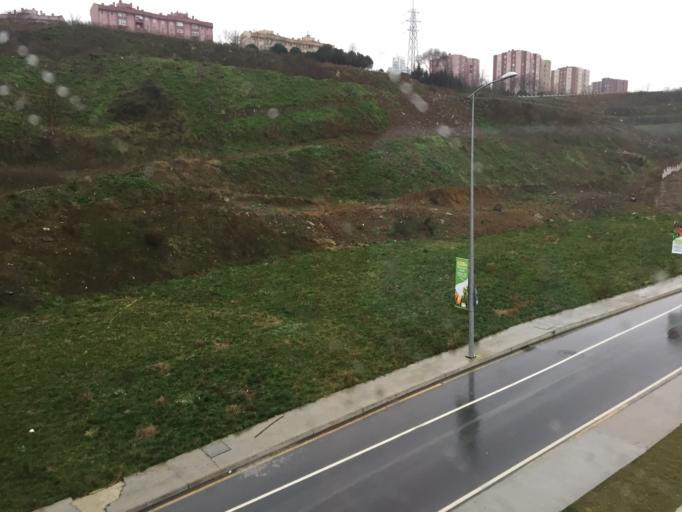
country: TR
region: Istanbul
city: Sisli
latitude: 41.1066
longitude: 28.9896
